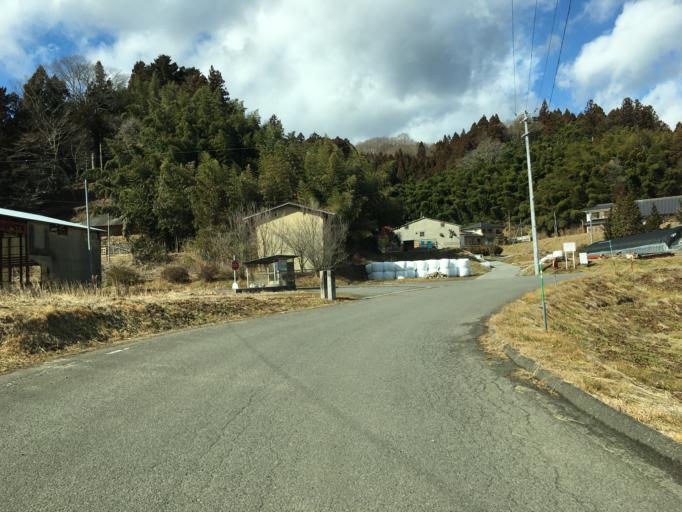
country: JP
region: Fukushima
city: Ishikawa
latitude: 37.2408
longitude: 140.5858
